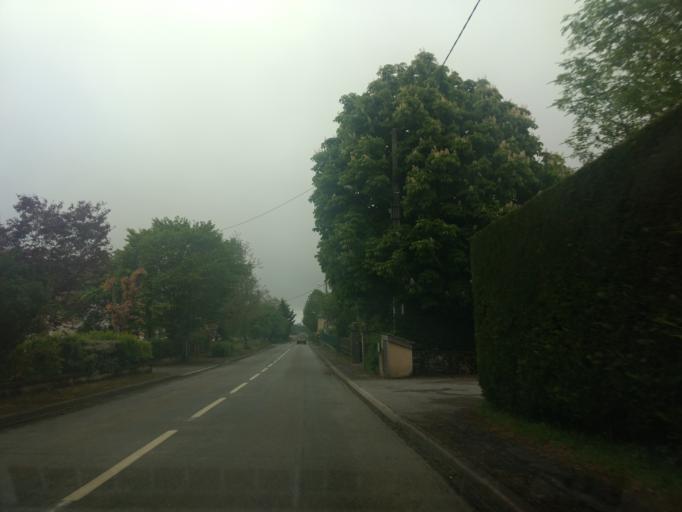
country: FR
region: Midi-Pyrenees
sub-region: Departement de l'Aveyron
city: Montbazens
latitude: 44.4557
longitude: 2.2506
